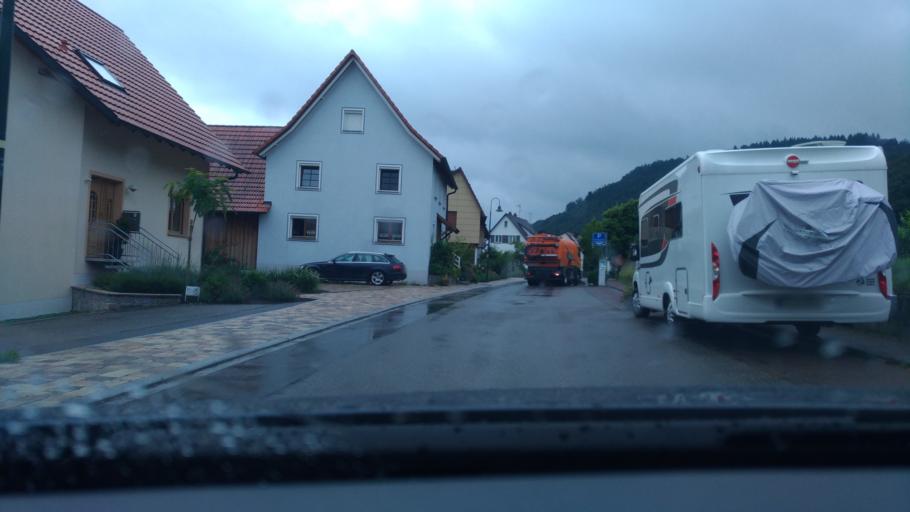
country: DE
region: Baden-Wuerttemberg
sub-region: Freiburg Region
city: Bodman-Ludwigshafen
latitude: 47.7994
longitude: 9.0389
